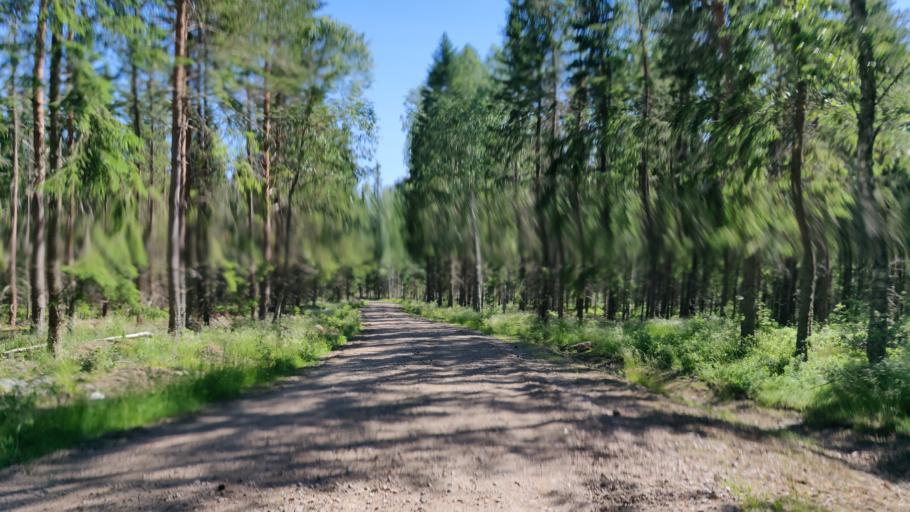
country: SE
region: Vaermland
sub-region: Hagfors Kommun
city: Hagfors
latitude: 59.9755
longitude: 13.6014
